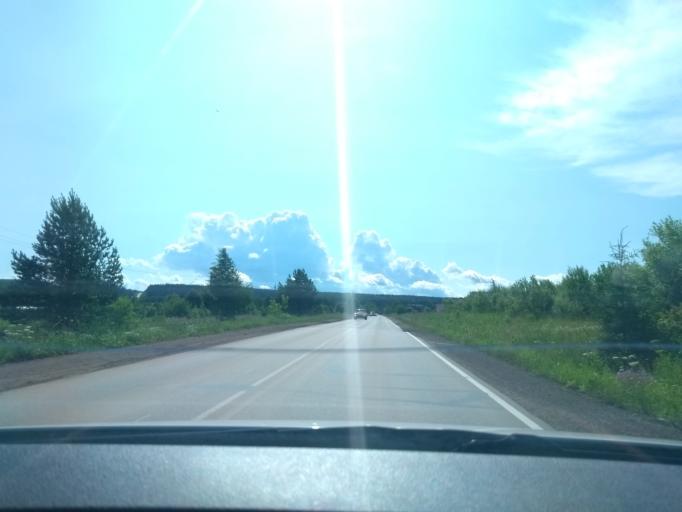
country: RU
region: Perm
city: Lobanovo
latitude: 57.8441
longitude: 56.3618
